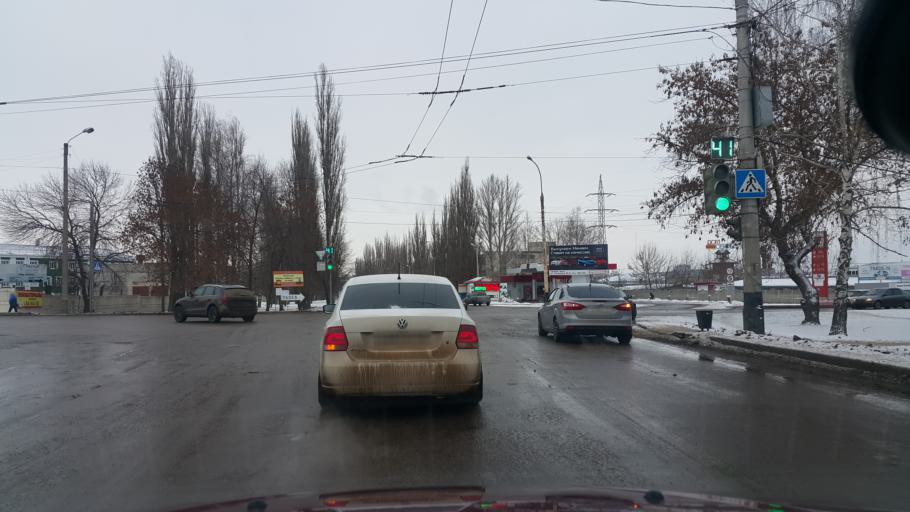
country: RU
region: Tambov
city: Tambov
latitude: 52.7330
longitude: 41.4019
